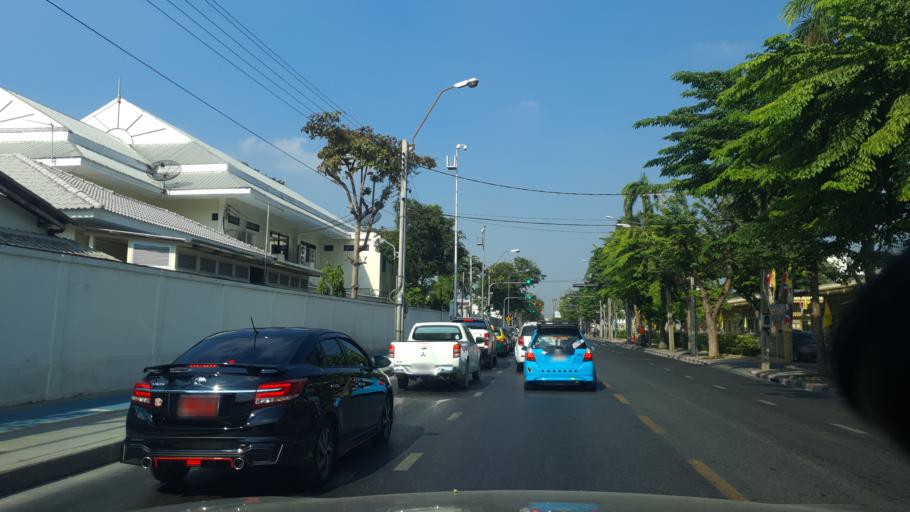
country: TH
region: Bangkok
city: Dusit
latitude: 13.7749
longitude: 100.5162
